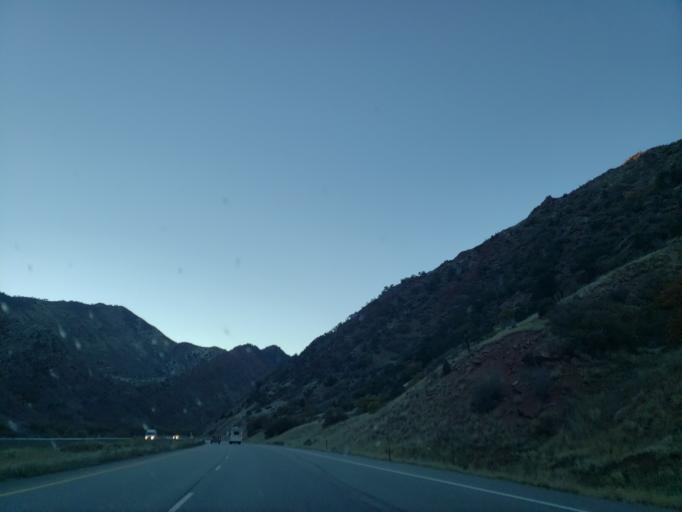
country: US
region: Colorado
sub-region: Garfield County
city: Glenwood Springs
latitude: 39.5656
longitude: -107.4157
